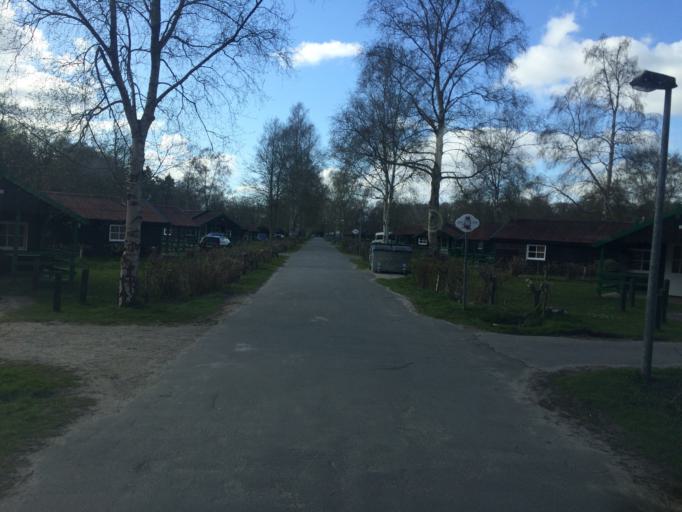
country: DE
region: Lower Saxony
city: Haren
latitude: 52.7960
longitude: 7.1991
